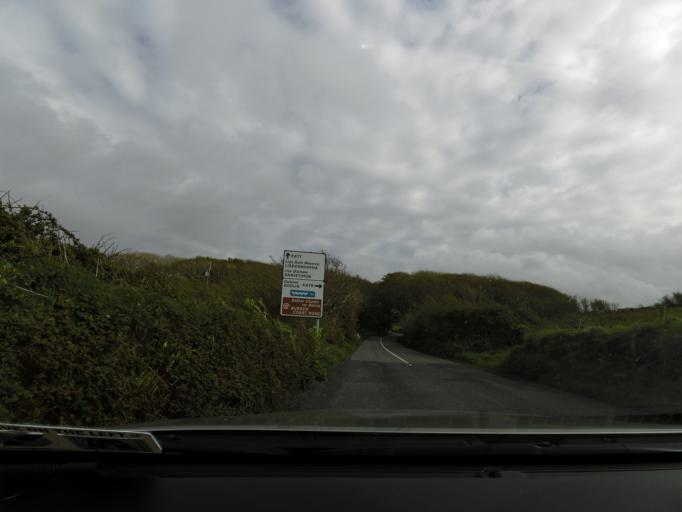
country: IE
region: Connaught
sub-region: County Galway
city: Bearna
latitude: 53.0474
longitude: -9.3421
